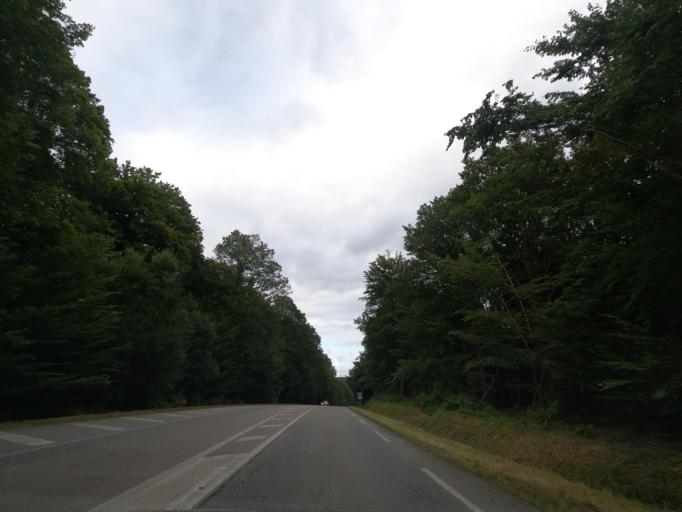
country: FR
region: Haute-Normandie
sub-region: Departement de l'Eure
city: Saint-Ouen-de-Thouberville
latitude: 49.3274
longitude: 0.9104
